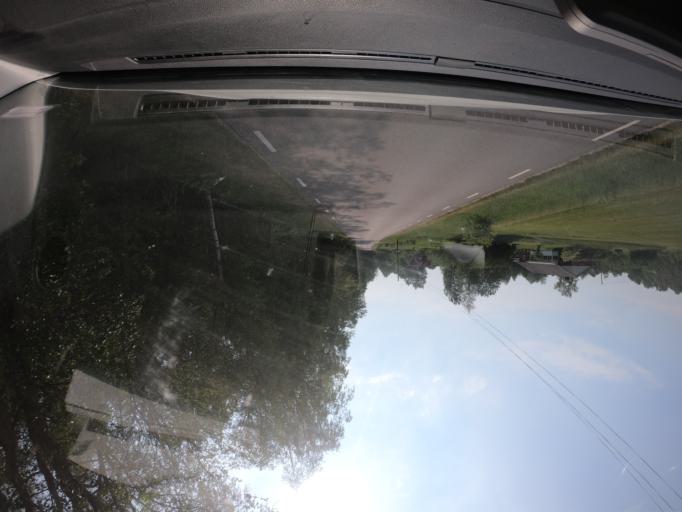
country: SE
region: Skane
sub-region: Hassleholms Kommun
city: Bjarnum
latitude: 56.3285
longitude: 13.6121
